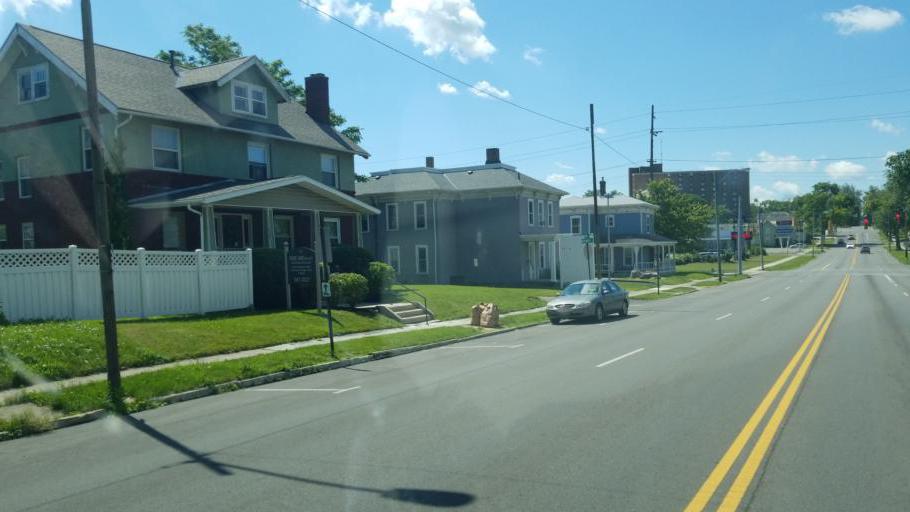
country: US
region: Ohio
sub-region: Marion County
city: Marion
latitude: 40.5855
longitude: -83.1287
